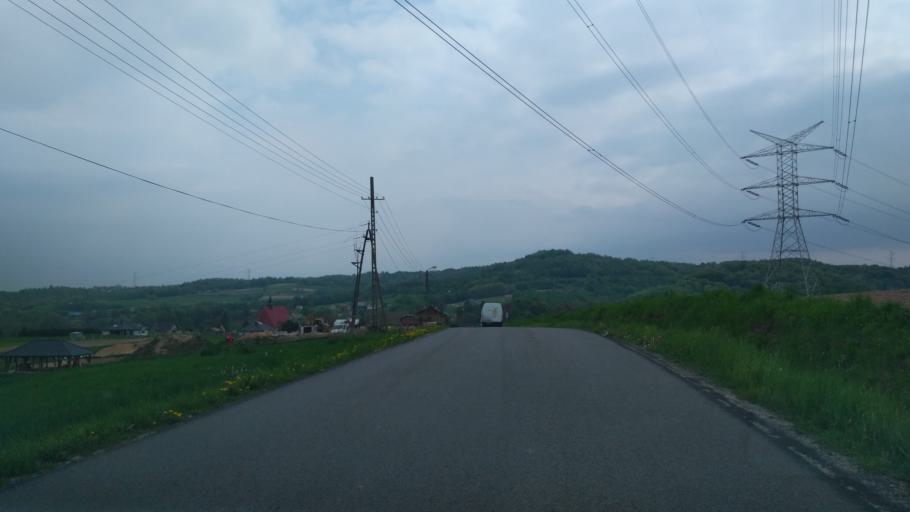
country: PL
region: Lesser Poland Voivodeship
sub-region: Powiat tarnowski
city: Tarnowiec
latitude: 49.9463
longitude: 21.0228
